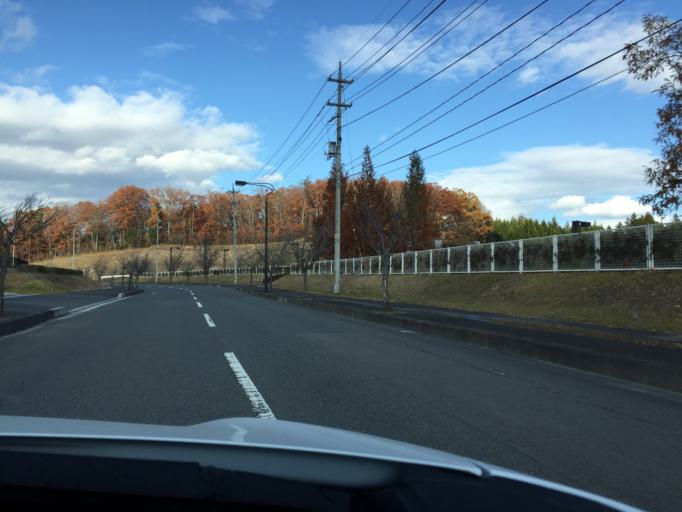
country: JP
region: Fukushima
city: Miharu
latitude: 37.4323
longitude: 140.5301
